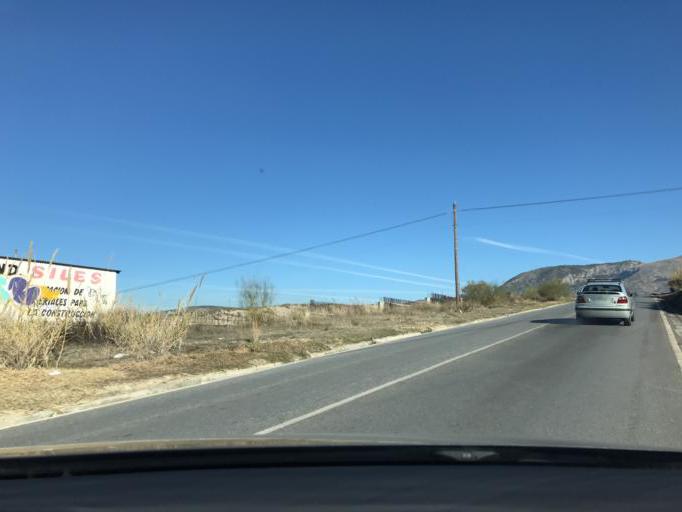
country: ES
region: Andalusia
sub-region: Provincia de Granada
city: Jun
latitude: 37.2195
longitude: -3.5863
